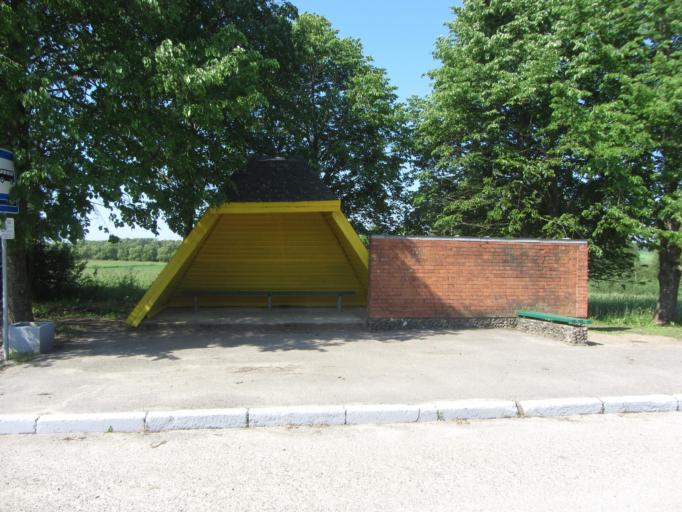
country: LT
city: Kaisiadorys
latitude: 54.9345
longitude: 24.4606
